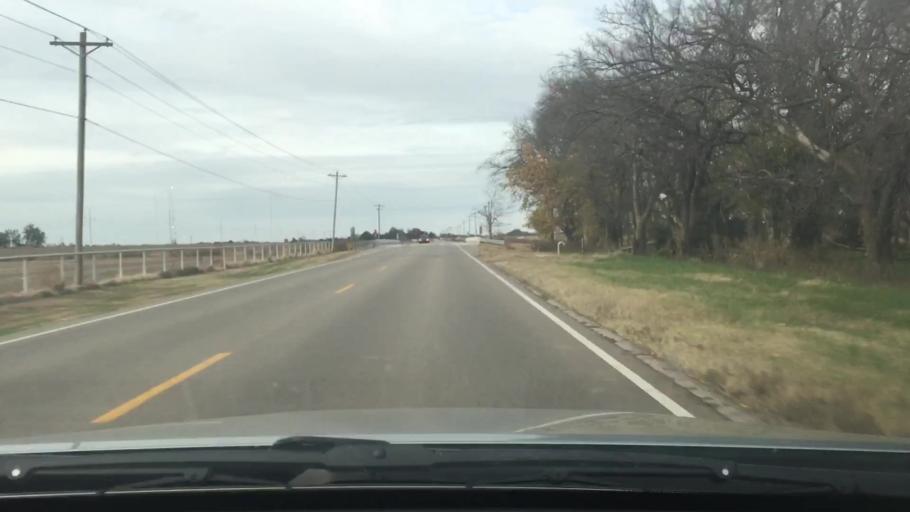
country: US
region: Kansas
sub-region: Sedgwick County
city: Maize
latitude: 37.7310
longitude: -97.4990
